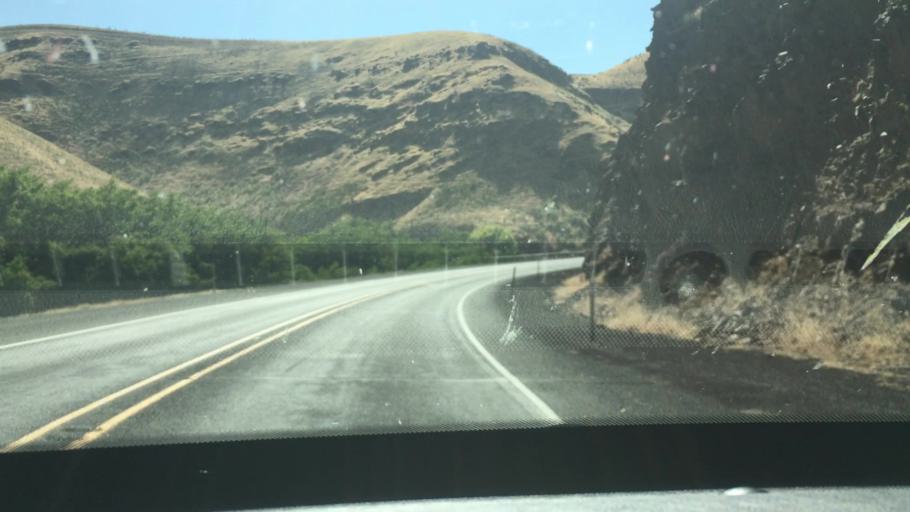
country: US
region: Washington
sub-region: Klickitat County
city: Goldendale
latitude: 45.6471
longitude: -120.8061
